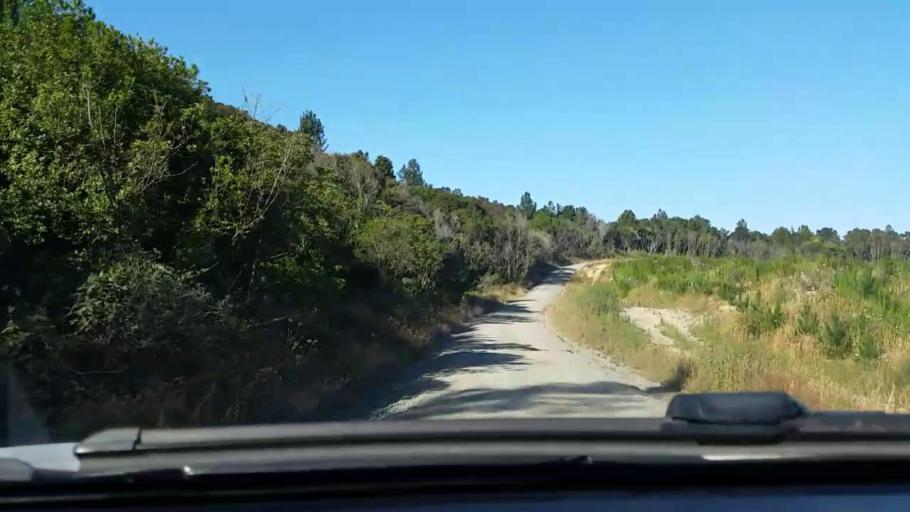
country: NZ
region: Bay of Plenty
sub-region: Kawerau District
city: Kawerau
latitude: -37.9909
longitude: 176.5301
